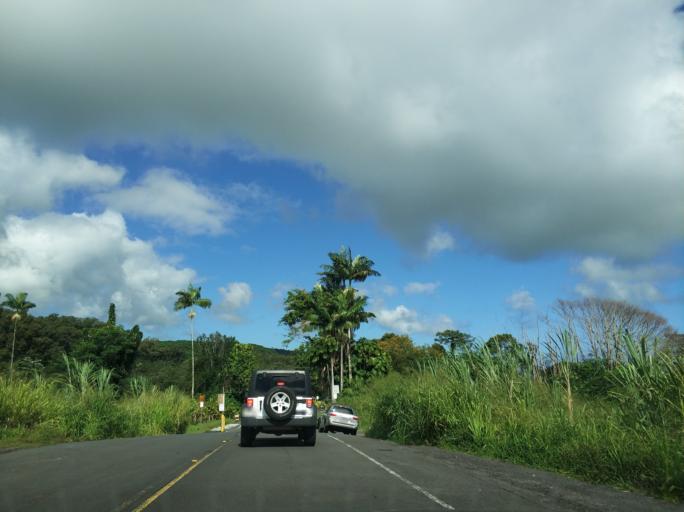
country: US
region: Hawaii
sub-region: Hawaii County
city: Pepeekeo
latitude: 19.8530
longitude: -155.1518
